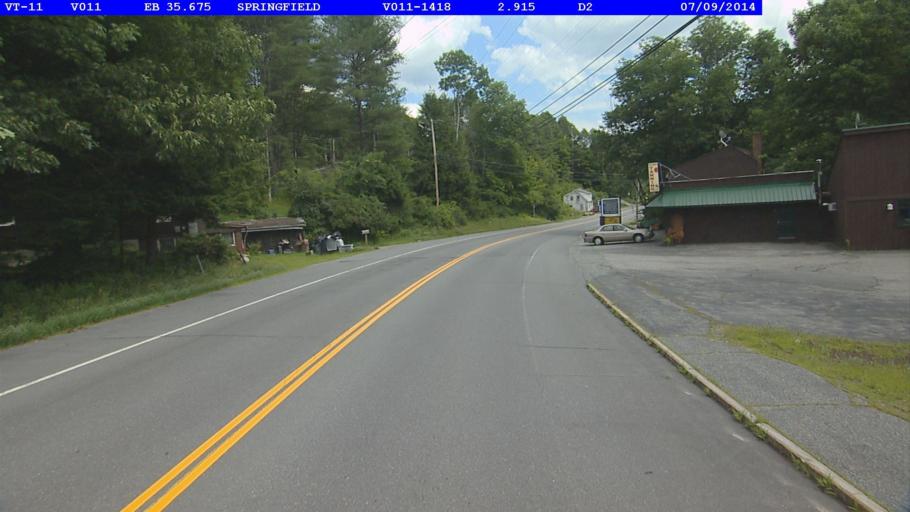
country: US
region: Vermont
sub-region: Windsor County
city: Springfield
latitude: 43.3010
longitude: -72.5057
